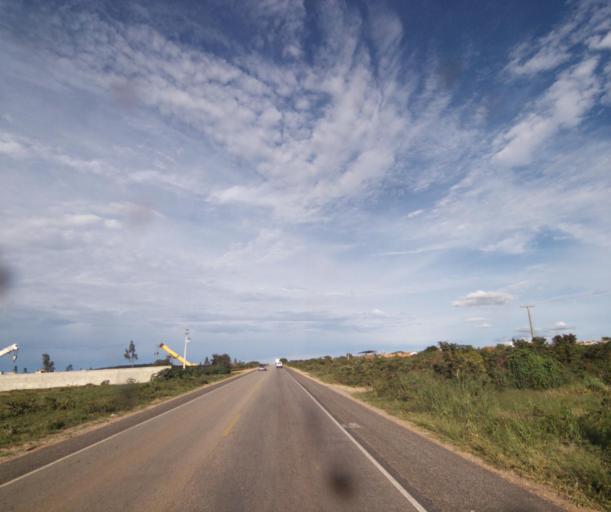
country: BR
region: Bahia
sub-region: Caetite
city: Caetite
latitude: -14.0688
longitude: -42.5331
